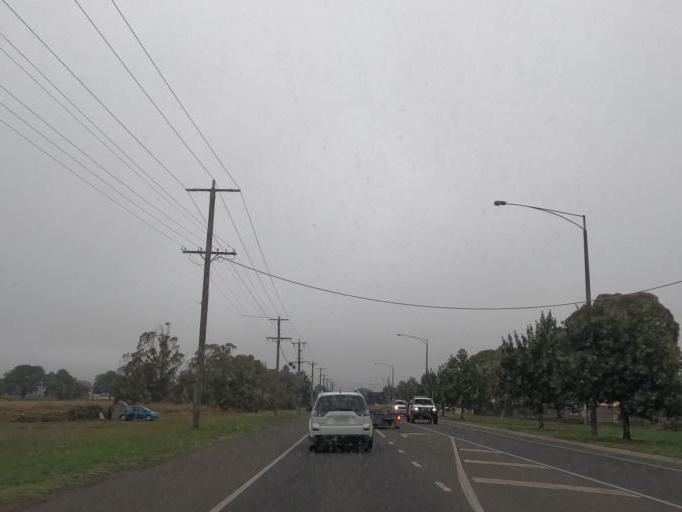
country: AU
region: Victoria
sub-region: Ballarat North
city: Newington
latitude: -37.5657
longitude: 143.8169
